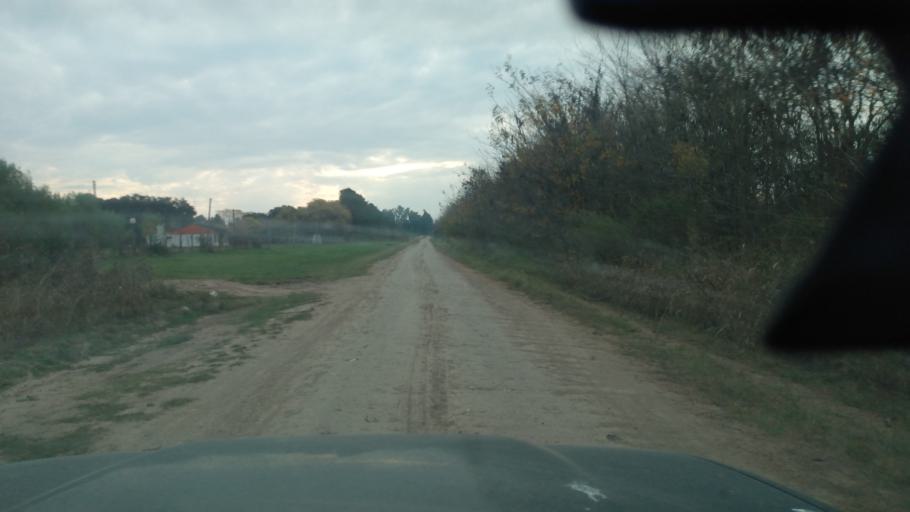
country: AR
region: Buenos Aires
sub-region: Partido de Lujan
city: Lujan
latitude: -34.5638
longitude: -59.1533
